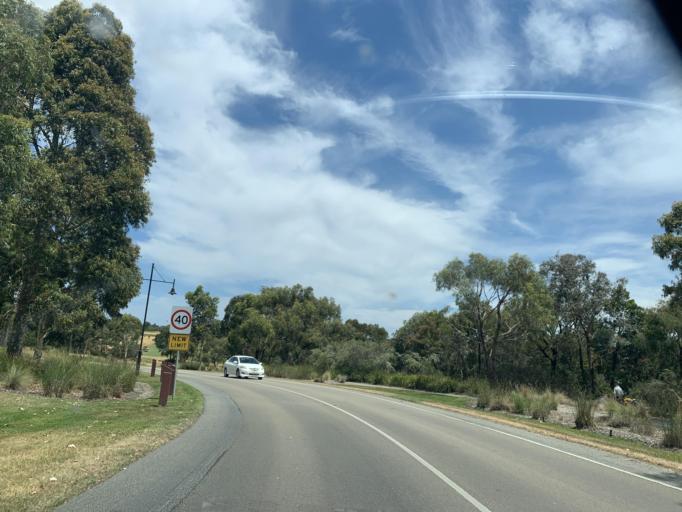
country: AU
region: Victoria
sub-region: Casey
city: Cranbourne South
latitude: -38.1320
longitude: 145.2507
